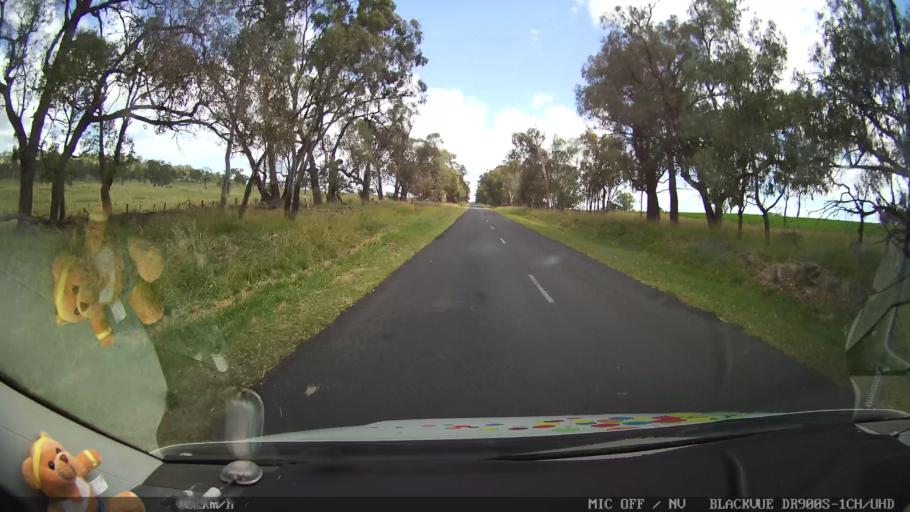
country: AU
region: New South Wales
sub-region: Glen Innes Severn
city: Glen Innes
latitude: -29.4830
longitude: 151.6841
